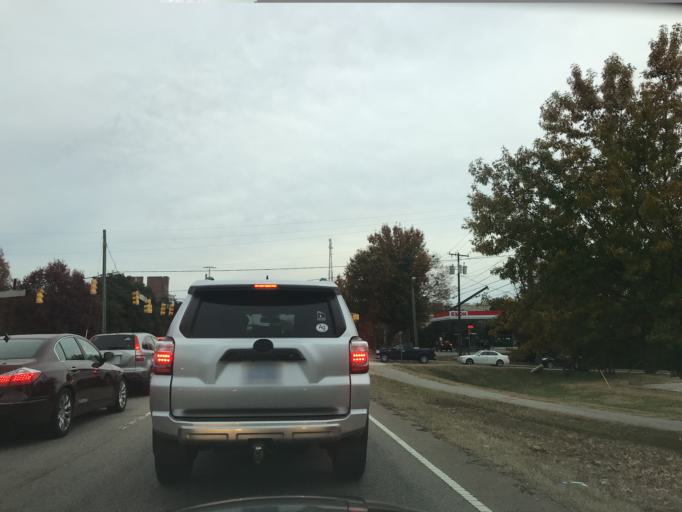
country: US
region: North Carolina
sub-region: Wake County
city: West Raleigh
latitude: 35.7823
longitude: -78.6794
